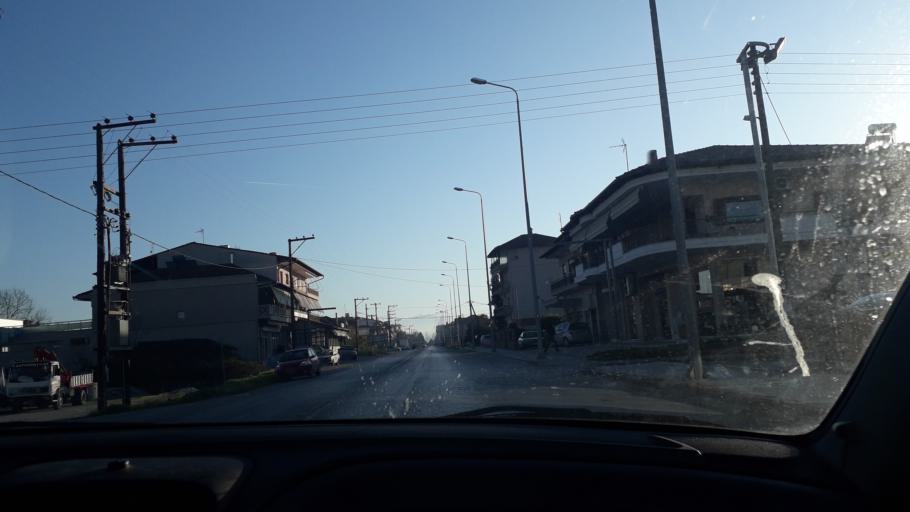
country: GR
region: Central Macedonia
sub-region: Nomos Imathias
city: Alexandreia
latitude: 40.6306
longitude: 22.4489
